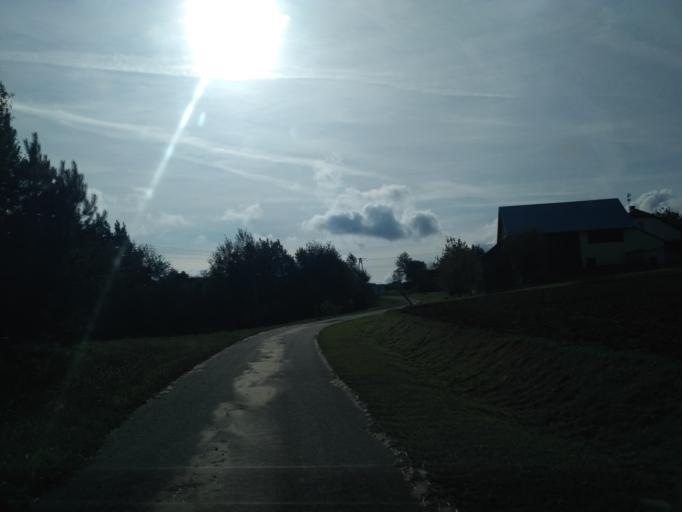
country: PL
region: Subcarpathian Voivodeship
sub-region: Powiat strzyzowski
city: Strzyzow
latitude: 49.8492
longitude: 21.8301
